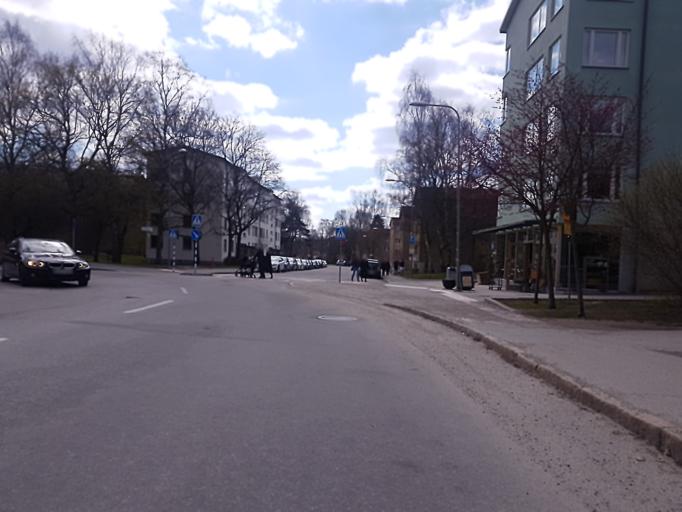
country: SE
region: Stockholm
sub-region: Stockholms Kommun
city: OEstermalm
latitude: 59.2948
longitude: 18.1066
